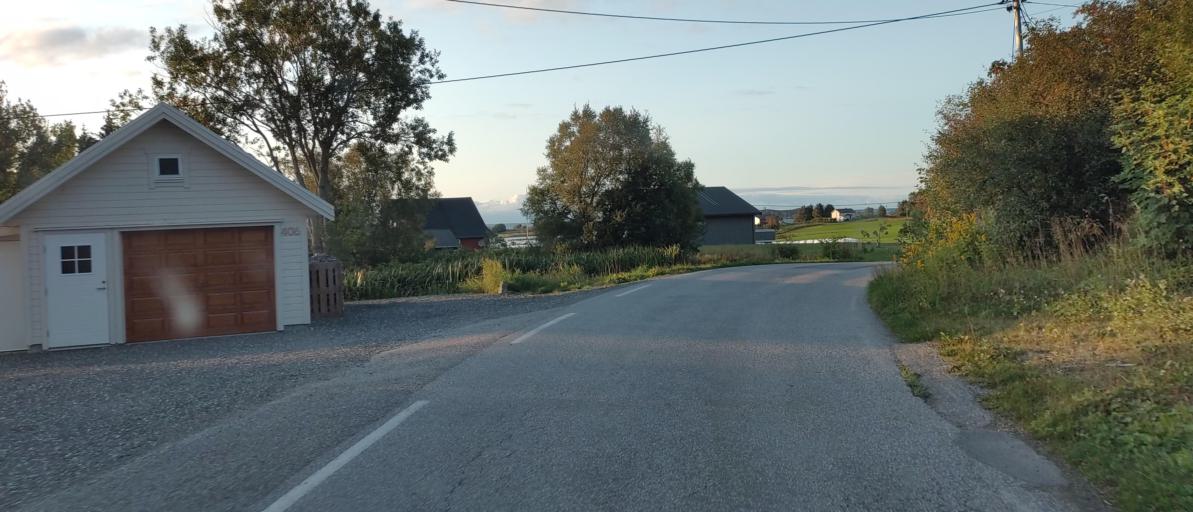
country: NO
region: More og Romsdal
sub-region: Fraena
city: Elnesvagen
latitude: 62.9944
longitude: 7.2202
